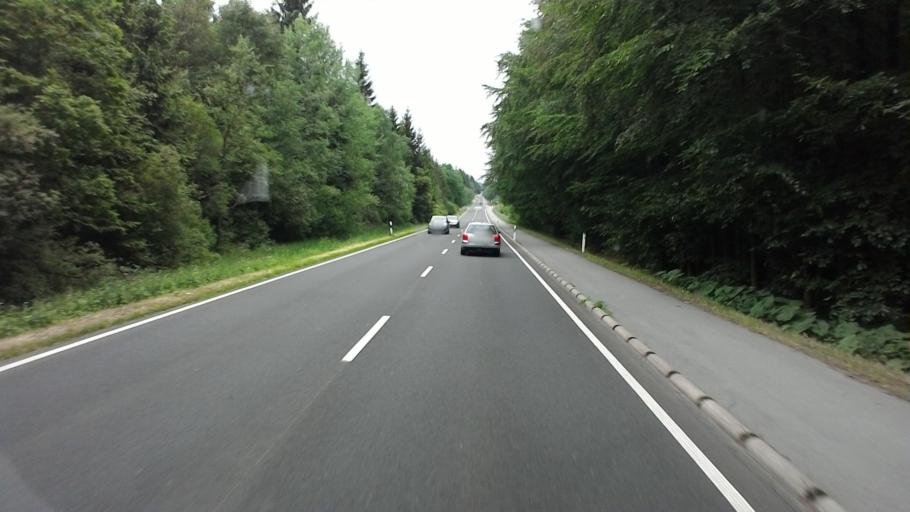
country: DE
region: North Rhine-Westphalia
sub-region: Regierungsbezirk Koln
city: Monschau
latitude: 50.6068
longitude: 6.2456
